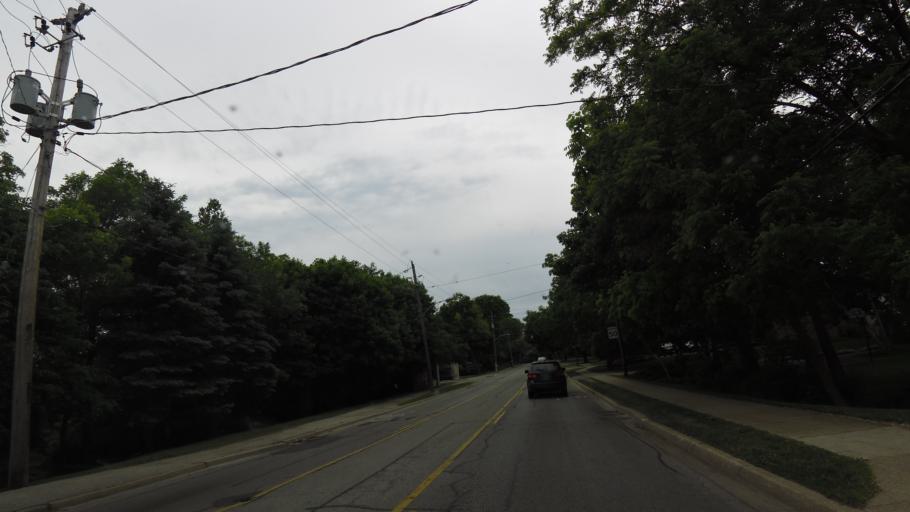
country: CA
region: Ontario
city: Burlington
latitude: 43.3545
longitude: -79.7532
